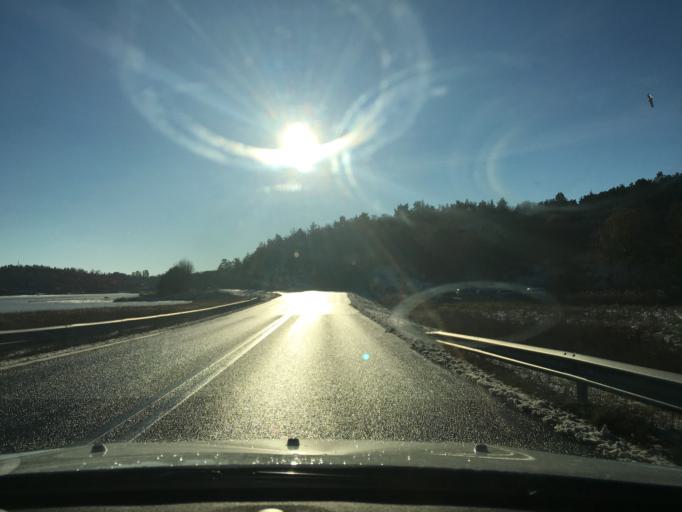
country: SE
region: Vaestra Goetaland
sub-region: Tjorns Kommun
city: Myggenas
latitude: 58.0766
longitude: 11.6963
